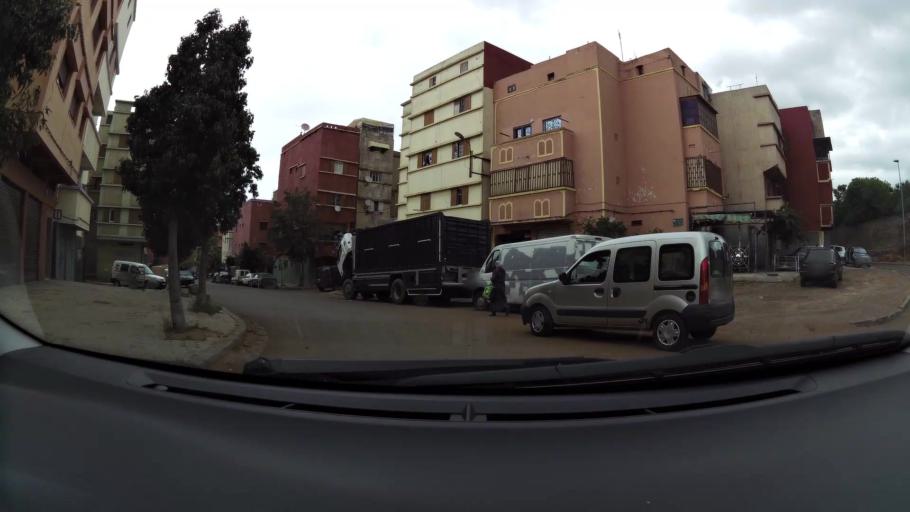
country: MA
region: Grand Casablanca
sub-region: Casablanca
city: Casablanca
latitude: 33.5588
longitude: -7.5588
